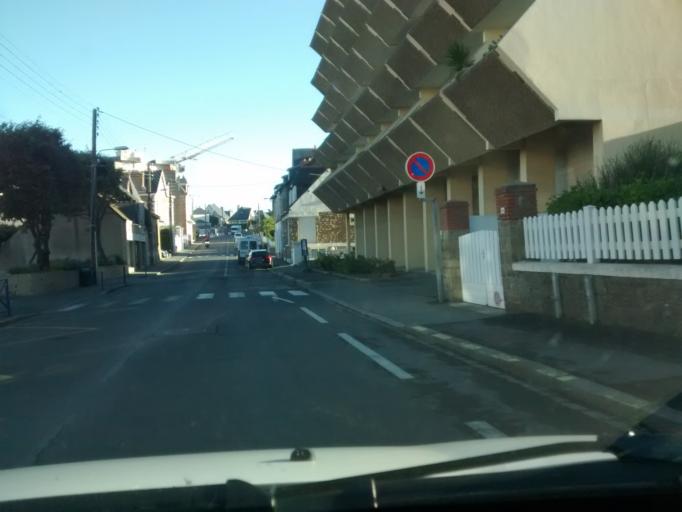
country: FR
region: Brittany
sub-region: Departement d'Ille-et-Vilaine
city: Saint-Malo
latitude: 48.6634
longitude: -1.9883
